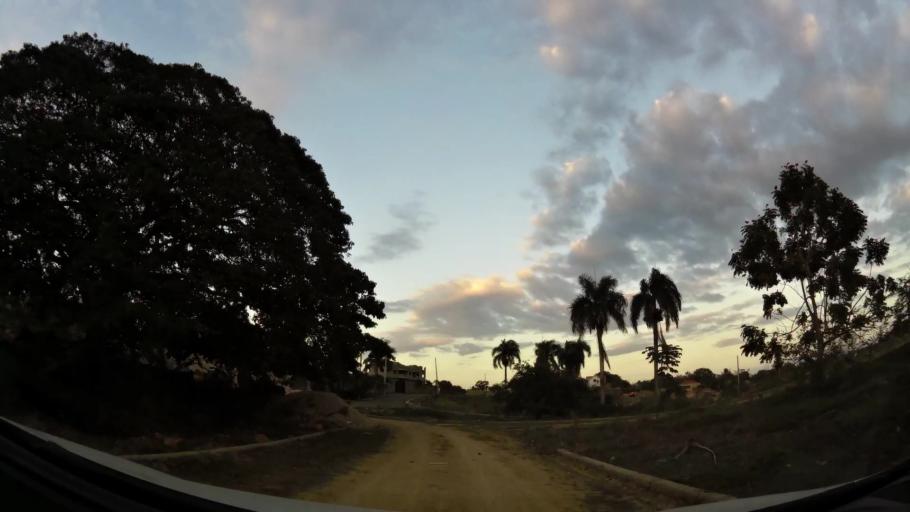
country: DO
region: Nacional
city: La Agustina
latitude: 18.5694
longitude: -69.9381
